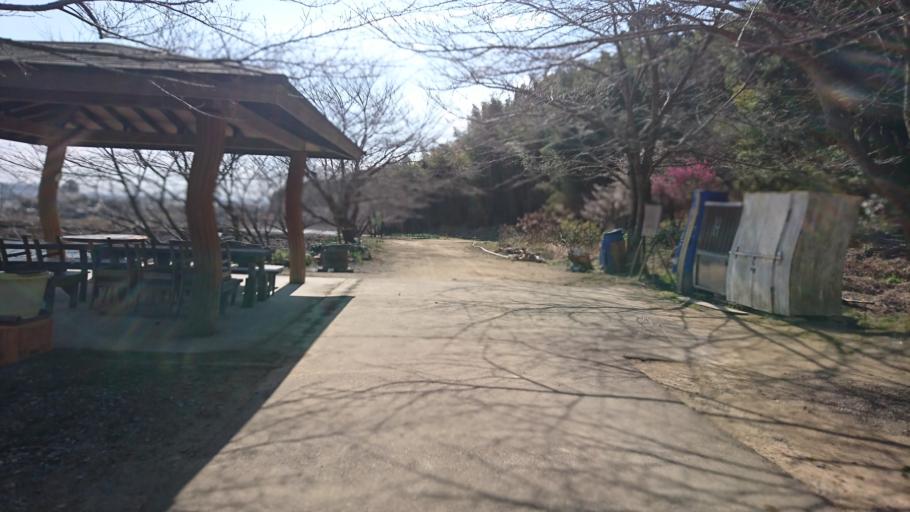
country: JP
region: Hyogo
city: Kakogawacho-honmachi
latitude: 34.8259
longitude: 134.7995
